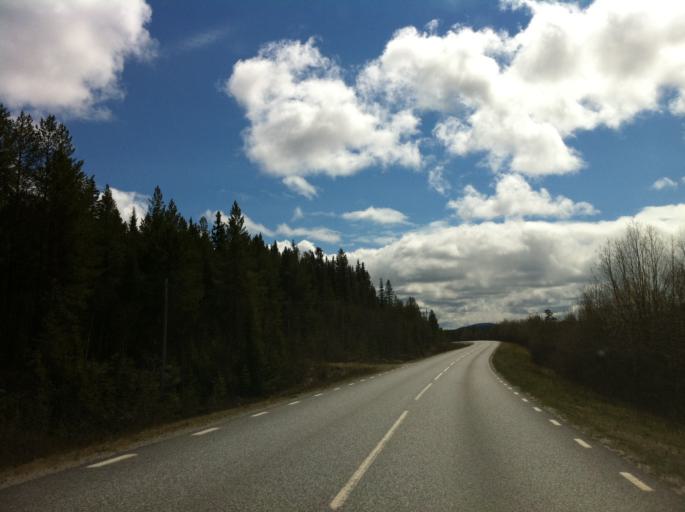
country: SE
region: Jaemtland
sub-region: Are Kommun
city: Are
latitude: 62.5869
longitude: 12.5536
